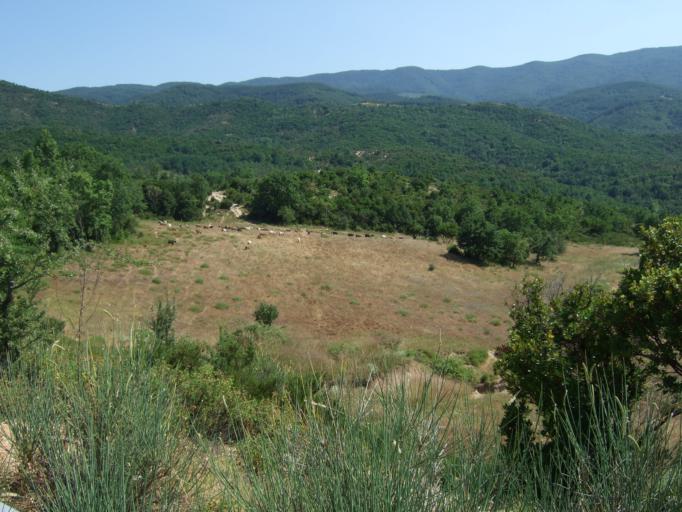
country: GR
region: Central Macedonia
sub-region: Nomos Chalkidikis
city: Arnaia
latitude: 40.5052
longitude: 23.5447
